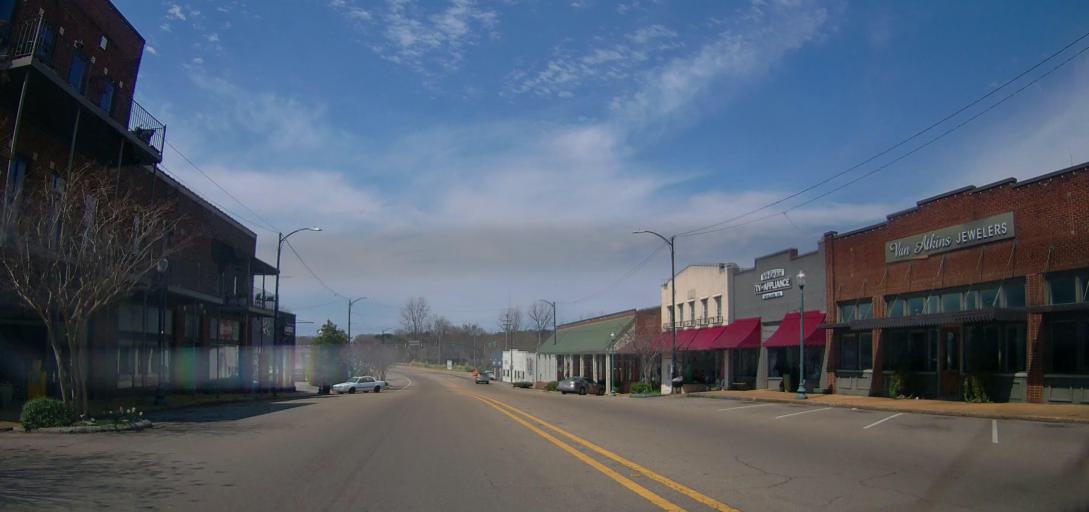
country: US
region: Mississippi
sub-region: Union County
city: New Albany
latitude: 34.4944
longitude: -89.0095
